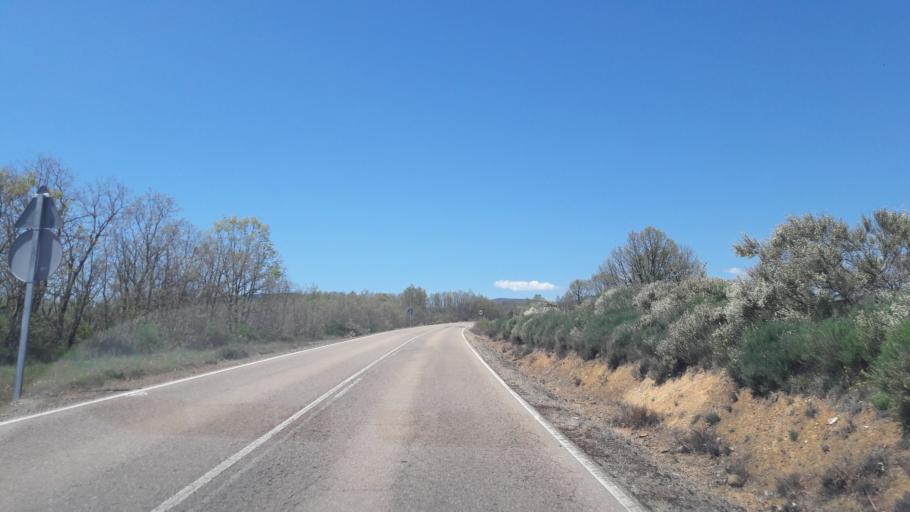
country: ES
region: Castille and Leon
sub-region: Provincia de Salamanca
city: Monleon
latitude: 40.5921
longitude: -5.8727
